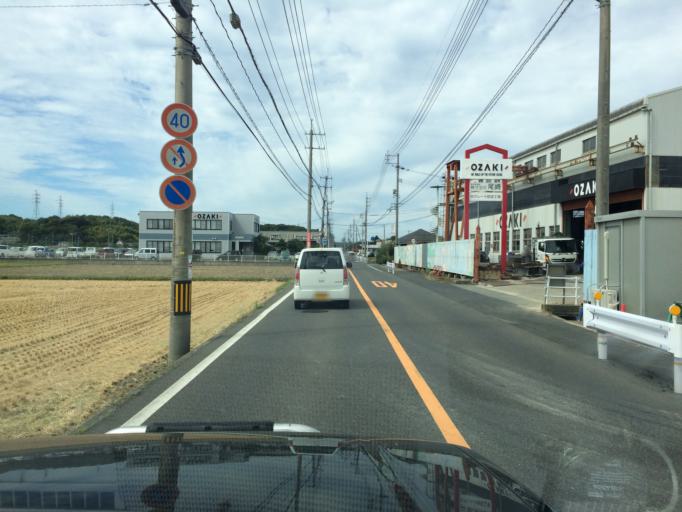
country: JP
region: Tottori
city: Tottori
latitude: 35.5014
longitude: 134.1963
